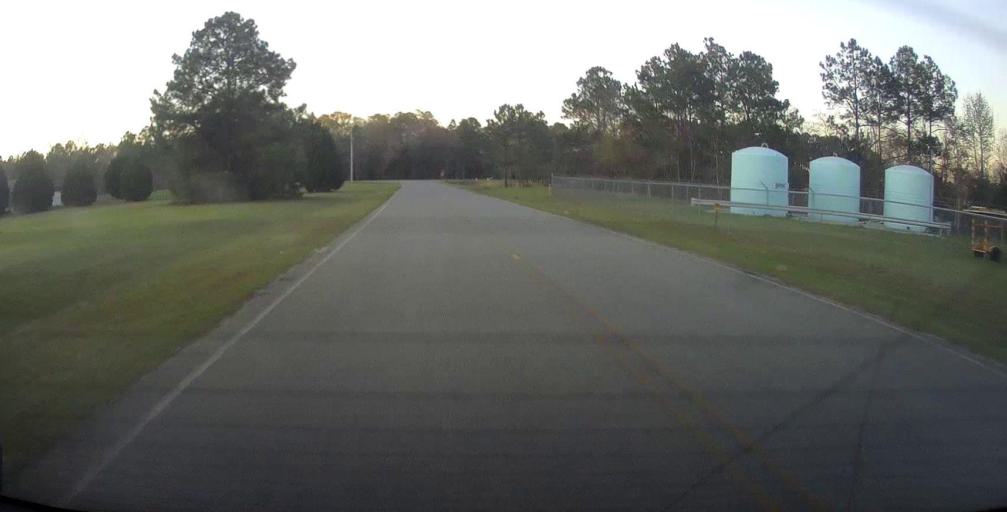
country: US
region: Georgia
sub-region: Crisp County
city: Cordele
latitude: 31.9269
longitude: -83.7802
